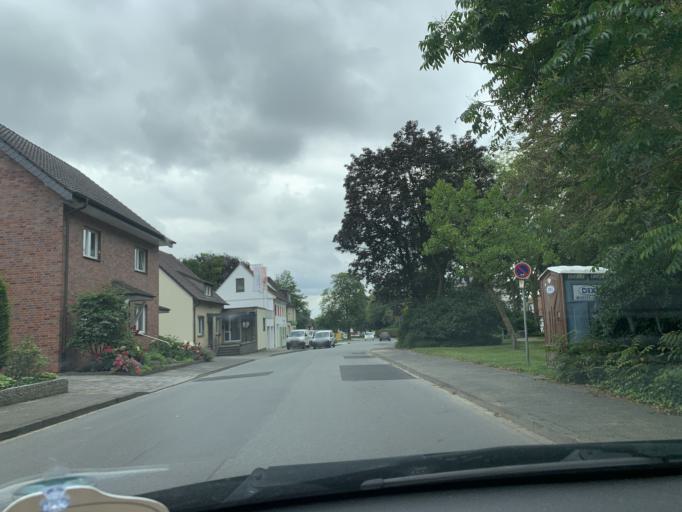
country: DE
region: North Rhine-Westphalia
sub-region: Regierungsbezirk Munster
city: Wadersloh
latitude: 51.7360
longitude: 8.2500
